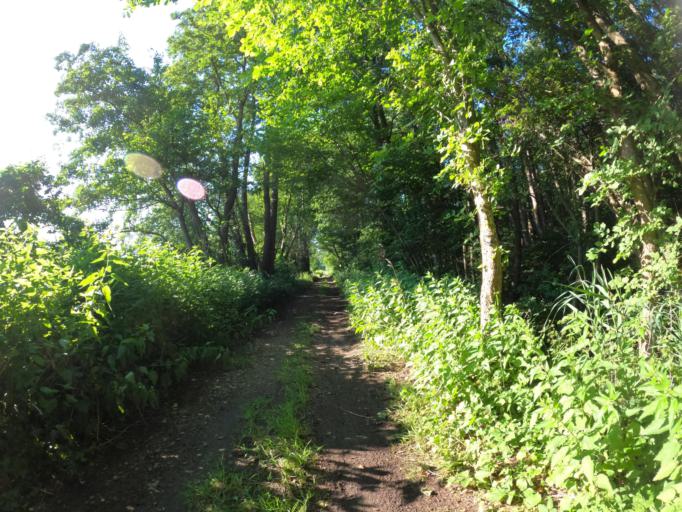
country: DE
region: Brandenburg
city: Gartz
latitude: 53.2350
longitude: 14.3662
